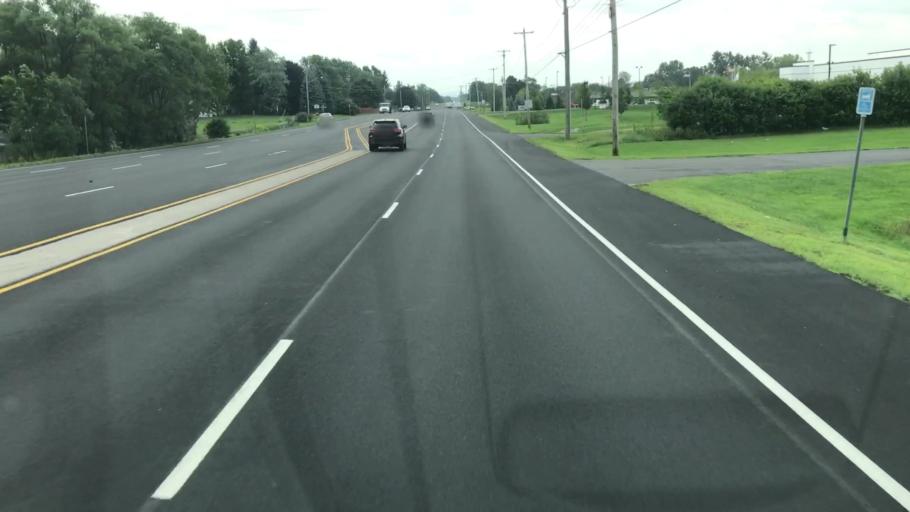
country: US
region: New York
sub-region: Onondaga County
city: Liverpool
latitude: 43.1405
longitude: -76.1876
